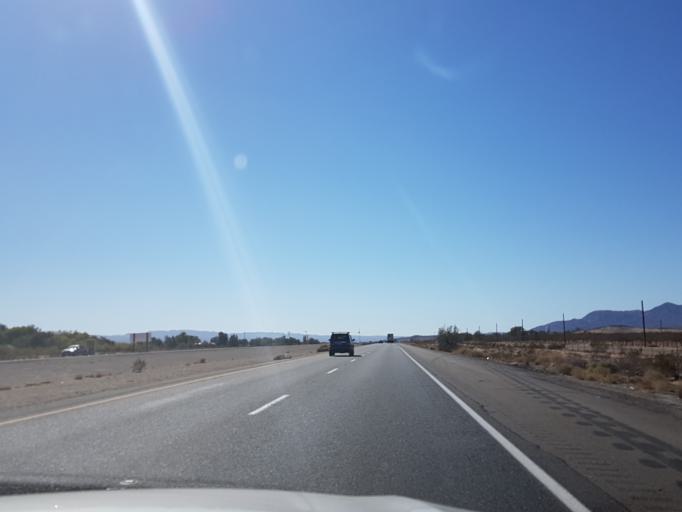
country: US
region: California
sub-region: San Bernardino County
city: Fort Irwin
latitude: 34.9550
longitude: -116.6651
